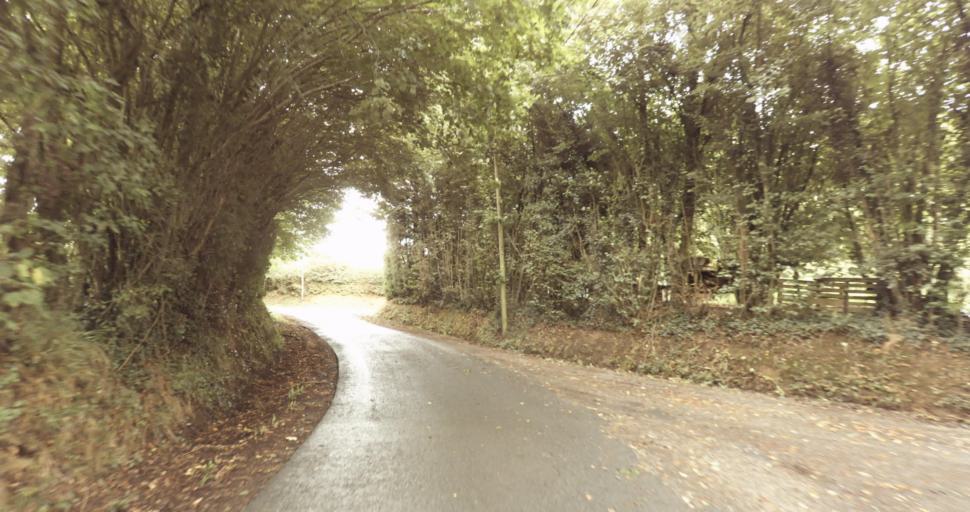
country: FR
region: Lower Normandy
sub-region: Departement de l'Orne
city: Sainte-Gauburge-Sainte-Colombe
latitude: 48.6976
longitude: 0.3676
